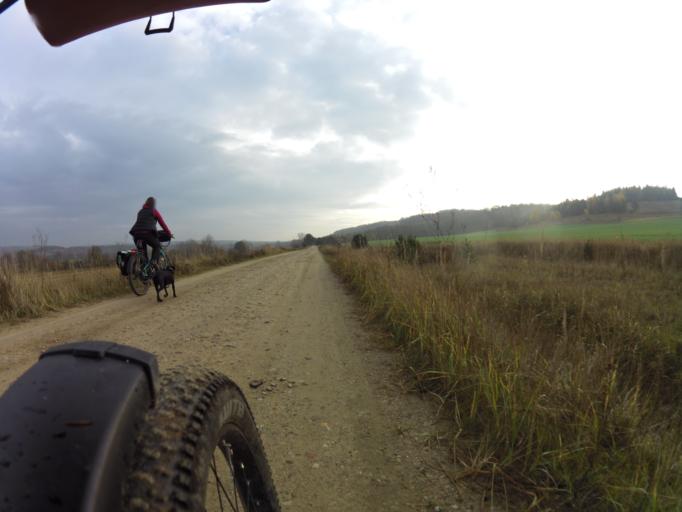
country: PL
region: Pomeranian Voivodeship
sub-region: Powiat wejherowski
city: Gniewino
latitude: 54.7081
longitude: 18.1007
